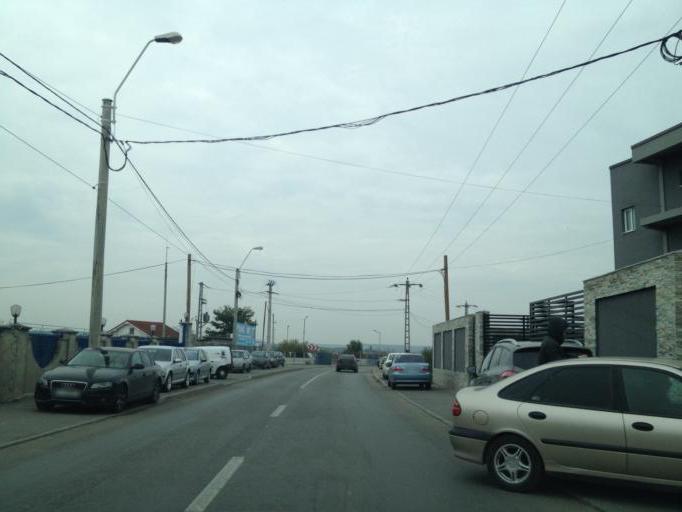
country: RO
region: Dolj
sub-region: Municipiul Craiova
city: Popoveni
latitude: 44.2869
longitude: 23.7963
